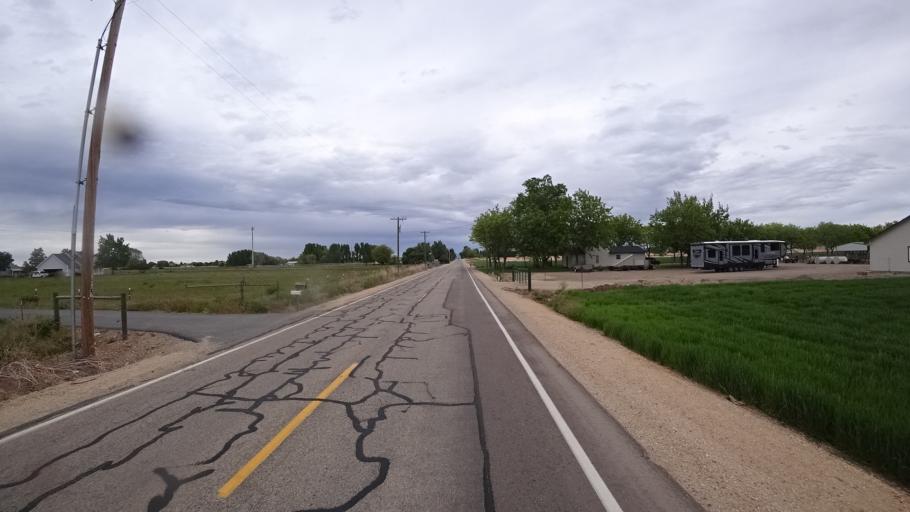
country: US
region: Idaho
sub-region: Ada County
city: Meridian
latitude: 43.5696
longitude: -116.4130
